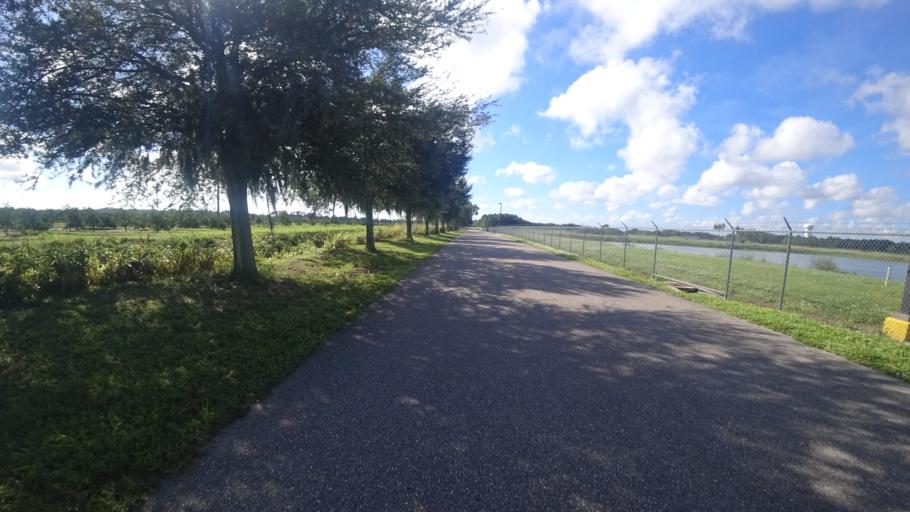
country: US
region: Florida
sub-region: Manatee County
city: Ellenton
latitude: 27.5820
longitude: -82.4746
